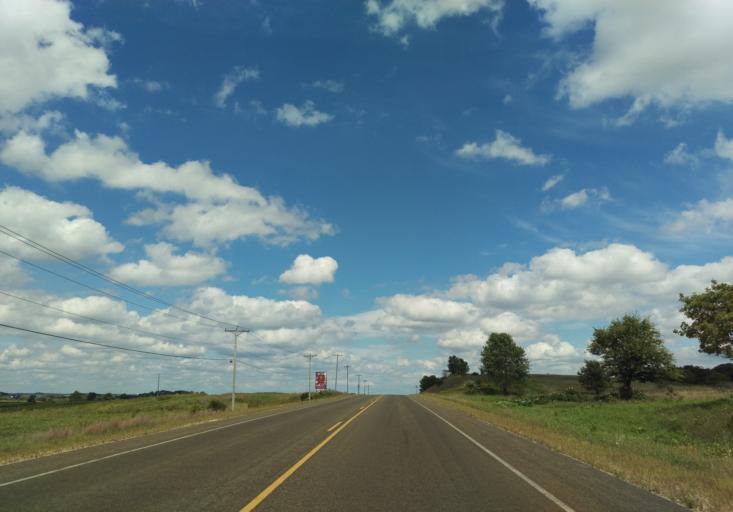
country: US
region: Wisconsin
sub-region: Dane County
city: Shorewood Hills
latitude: 43.1278
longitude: -89.4420
